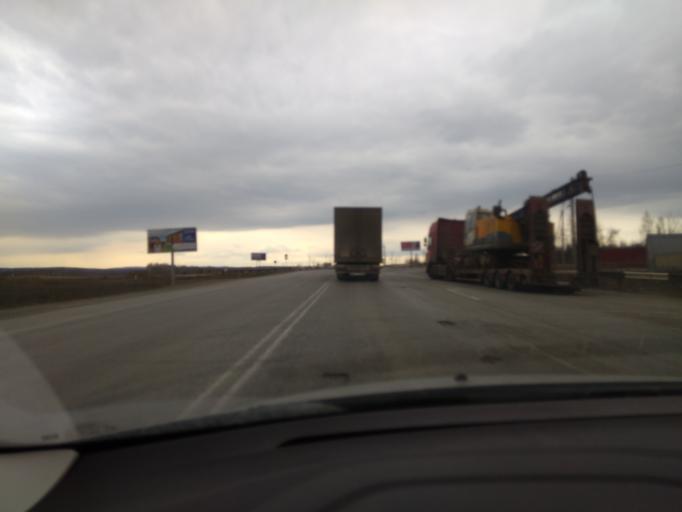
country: RU
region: Chelyabinsk
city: Chebarkul'
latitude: 54.9187
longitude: 60.3303
